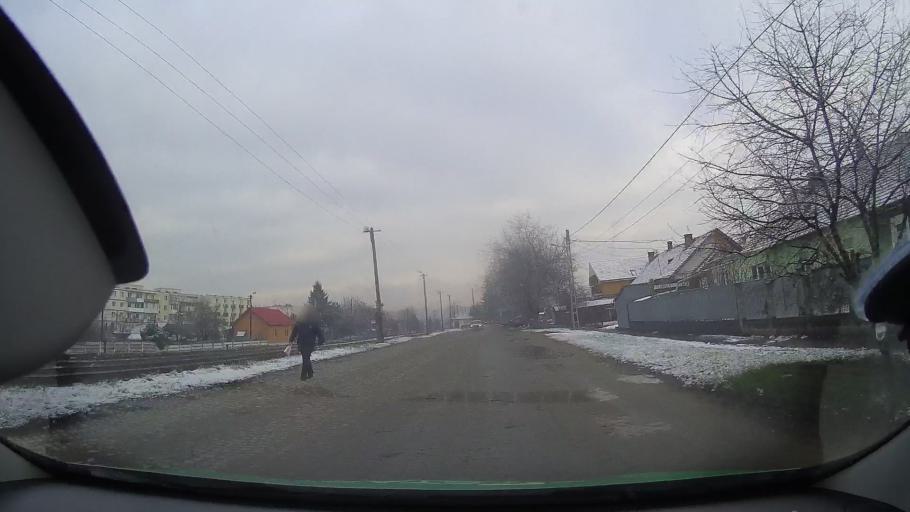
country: RO
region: Mures
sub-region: Comuna Ludus
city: Ludus
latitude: 46.4679
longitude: 24.0913
